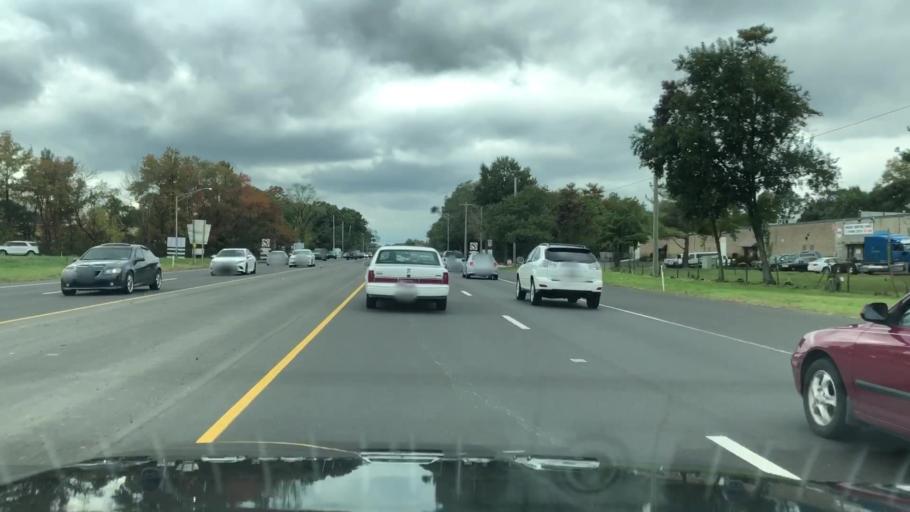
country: US
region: Pennsylvania
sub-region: Bucks County
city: Bristol
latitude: 40.1168
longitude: -74.8468
